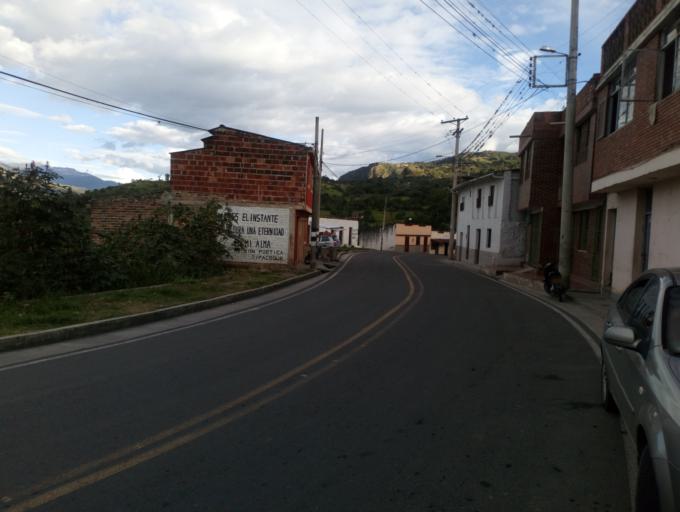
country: CO
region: Boyaca
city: Tipacoque
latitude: 6.4192
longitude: -72.6926
